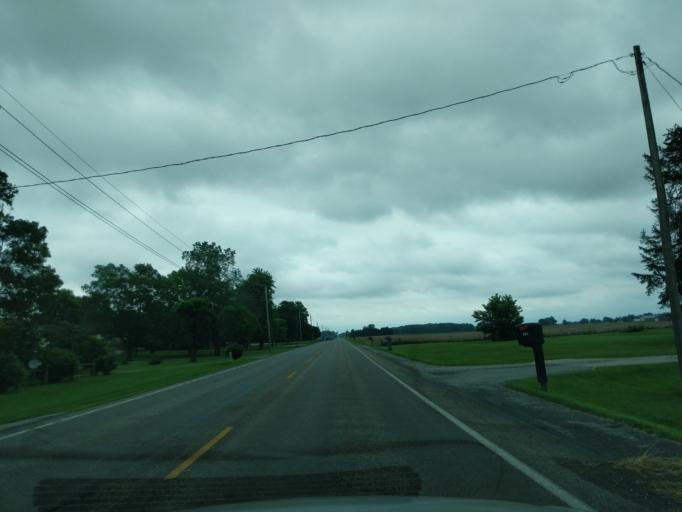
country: US
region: Indiana
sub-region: Tipton County
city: Tipton
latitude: 40.2834
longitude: -86.0018
